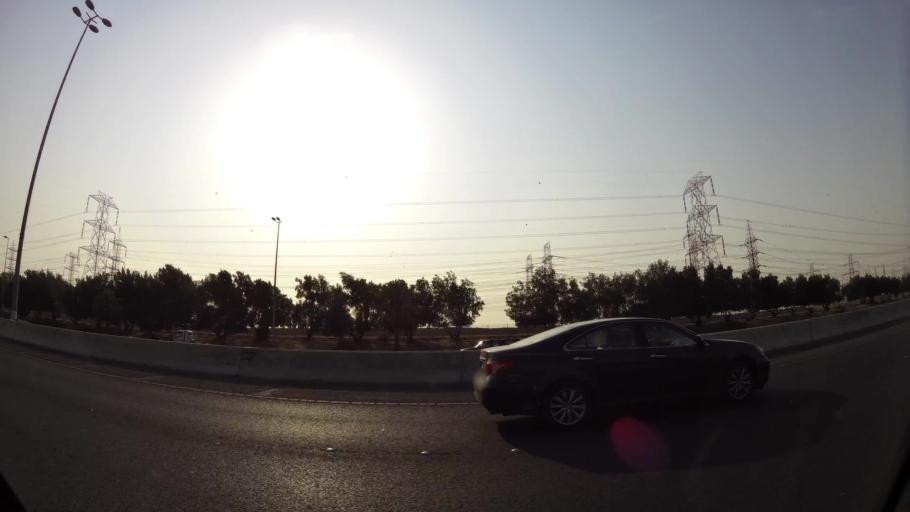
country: KW
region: Mubarak al Kabir
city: Sabah as Salim
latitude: 29.2580
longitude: 48.0446
